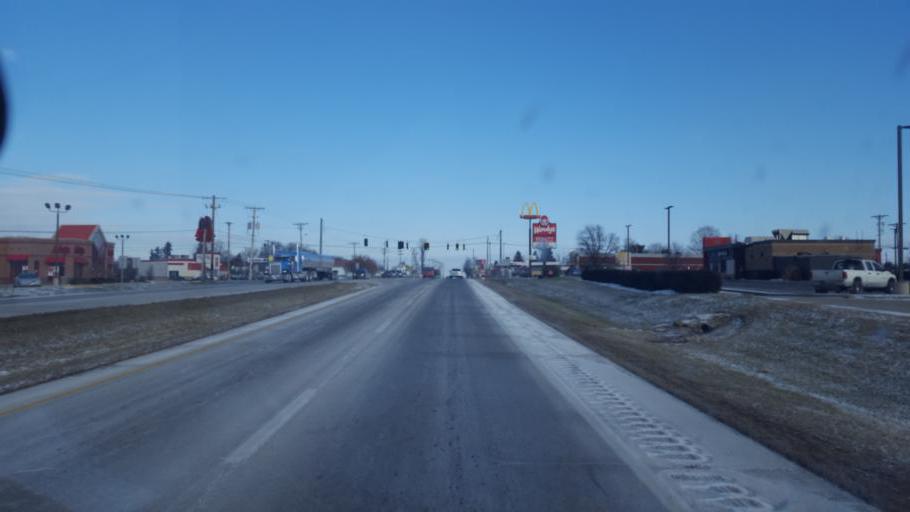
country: US
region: Ohio
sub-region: Pickaway County
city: South Bloomfield
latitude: 39.7135
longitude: -82.9870
